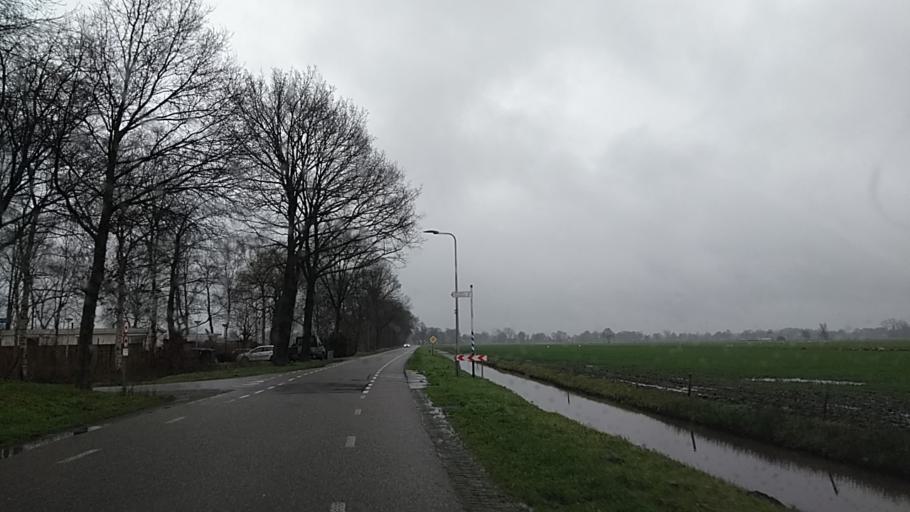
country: NL
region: Overijssel
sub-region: Gemeente Staphorst
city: Staphorst
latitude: 52.6111
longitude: 6.1779
